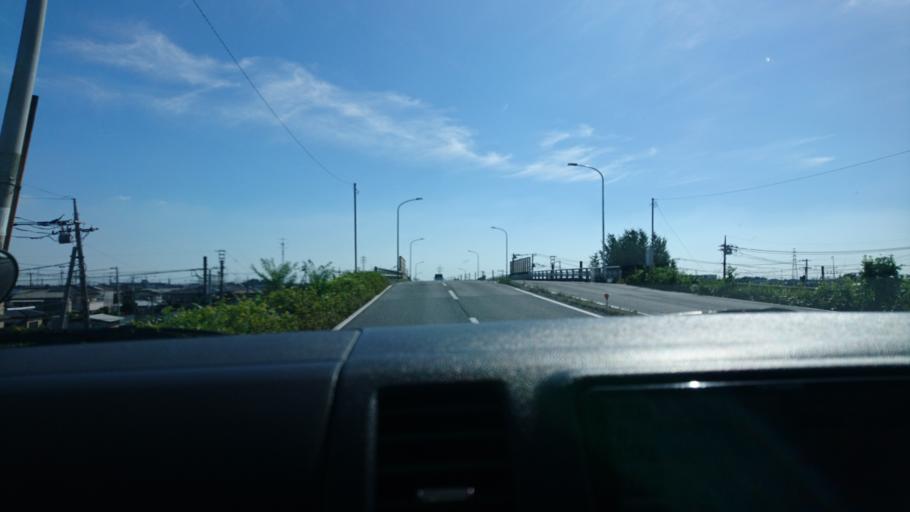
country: JP
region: Saitama
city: Kurihashi
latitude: 36.1268
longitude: 139.6952
